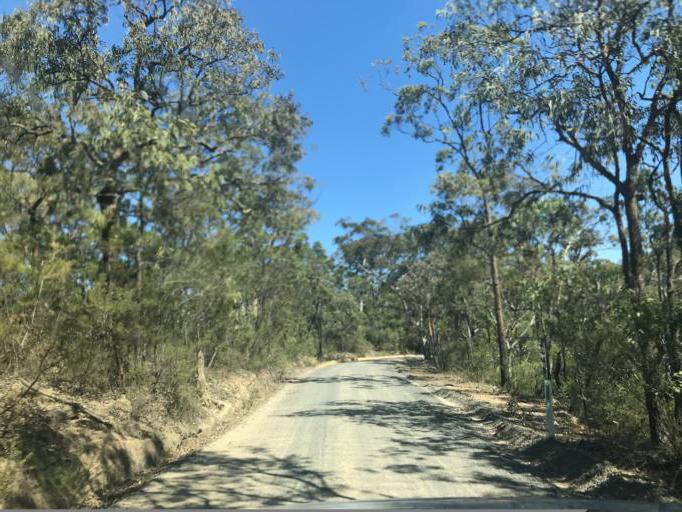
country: AU
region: New South Wales
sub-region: Wyong Shire
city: Little Jilliby
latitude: -33.1456
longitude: 151.0880
